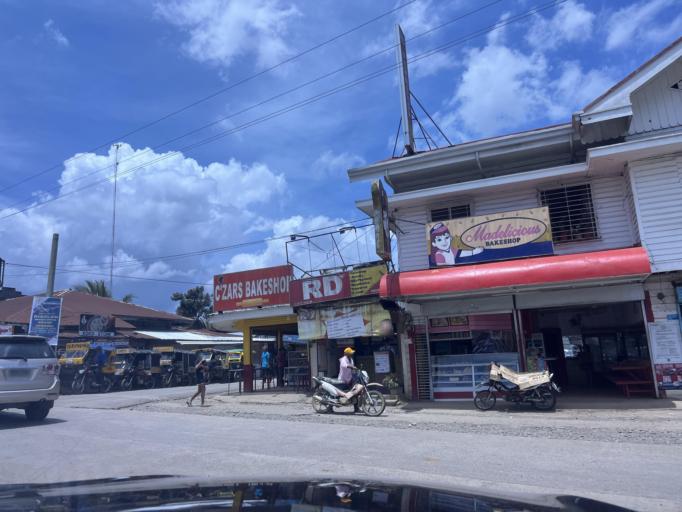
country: PH
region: Northern Mindanao
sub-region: Province of Bukidnon
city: Kisolon
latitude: 8.3278
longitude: 124.9783
